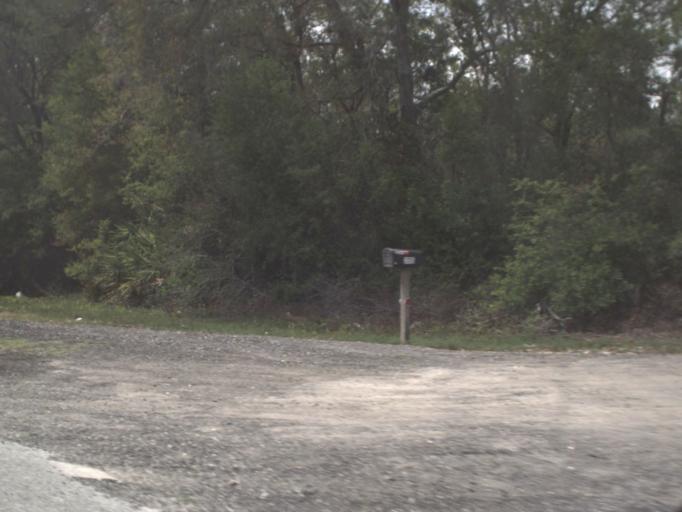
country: US
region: Florida
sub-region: Lake County
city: Lake Mack-Forest Hills
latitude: 28.9287
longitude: -81.4406
